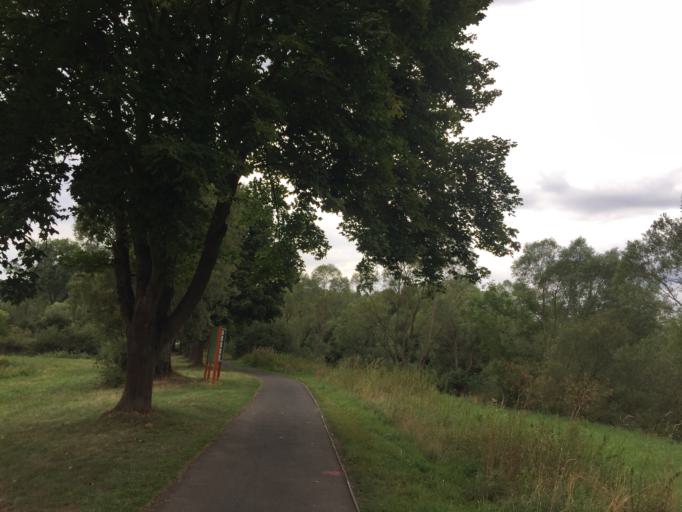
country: DE
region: Hesse
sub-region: Regierungsbezirk Kassel
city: Rotenburg an der Fulda
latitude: 50.9881
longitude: 9.7593
